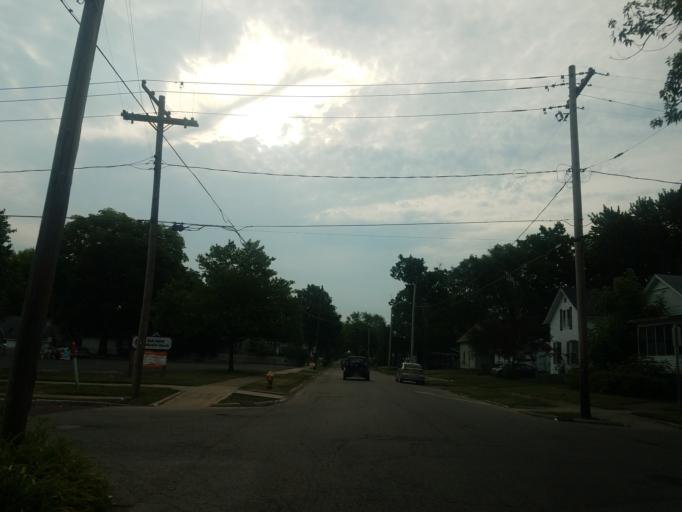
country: US
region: Illinois
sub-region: McLean County
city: Bloomington
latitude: 40.4728
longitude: -89.0020
